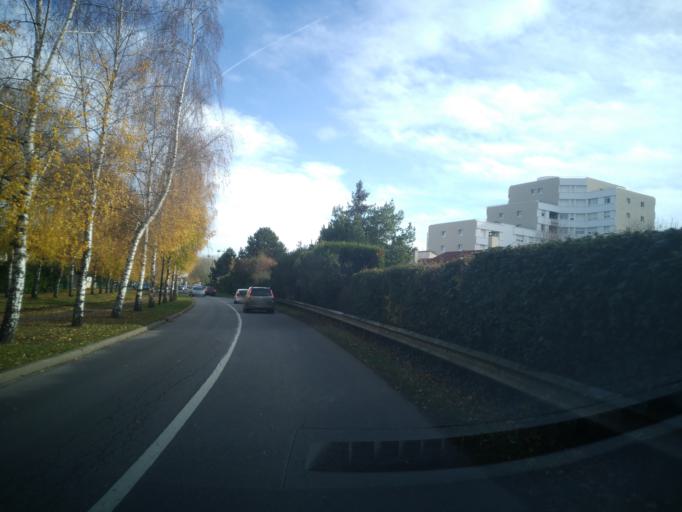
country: FR
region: Ile-de-France
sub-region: Departement des Yvelines
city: Plaisir
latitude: 48.8212
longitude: 1.9688
